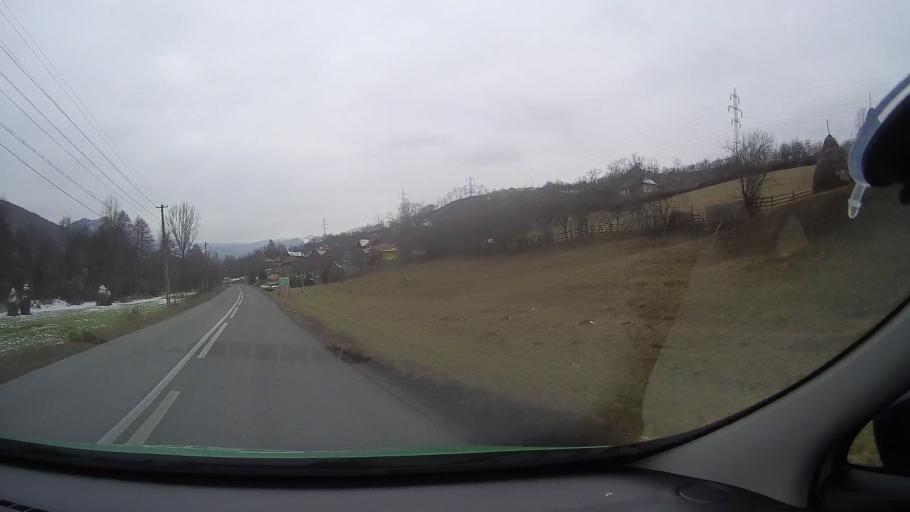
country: RO
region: Alba
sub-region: Comuna Metes
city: Metes
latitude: 46.1003
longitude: 23.4345
